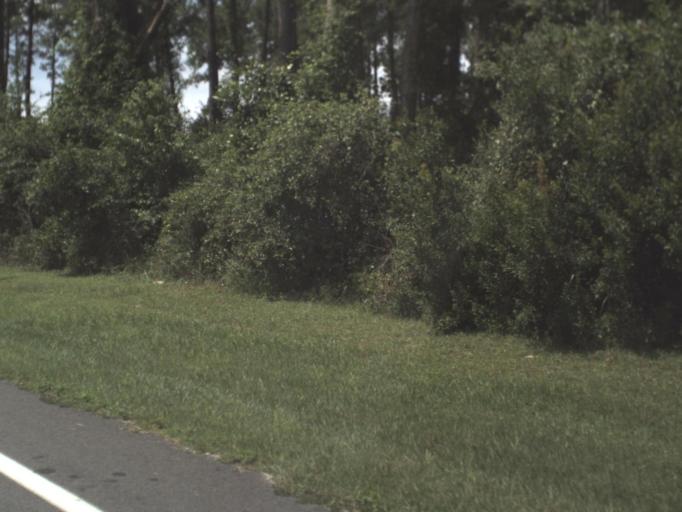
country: US
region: Florida
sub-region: Suwannee County
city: Wellborn
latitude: 30.3361
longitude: -82.7610
